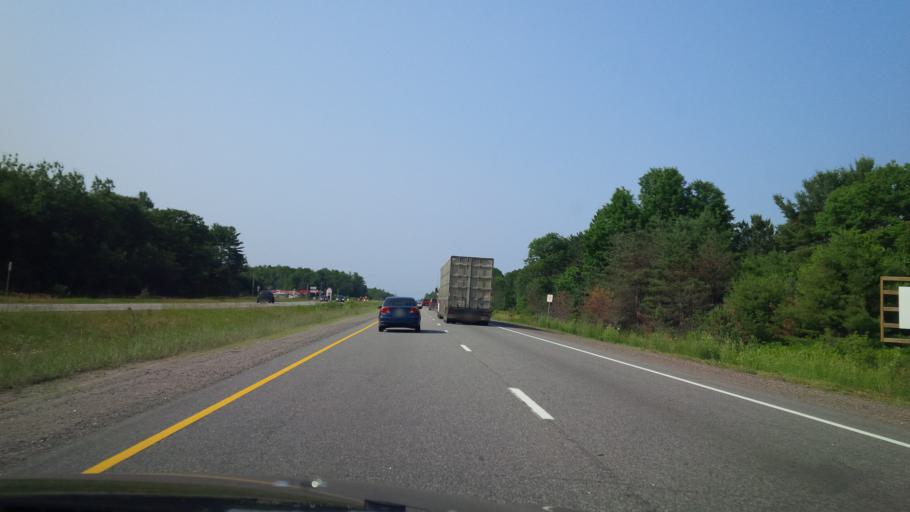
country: CA
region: Ontario
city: Bracebridge
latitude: 44.9836
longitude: -79.3131
